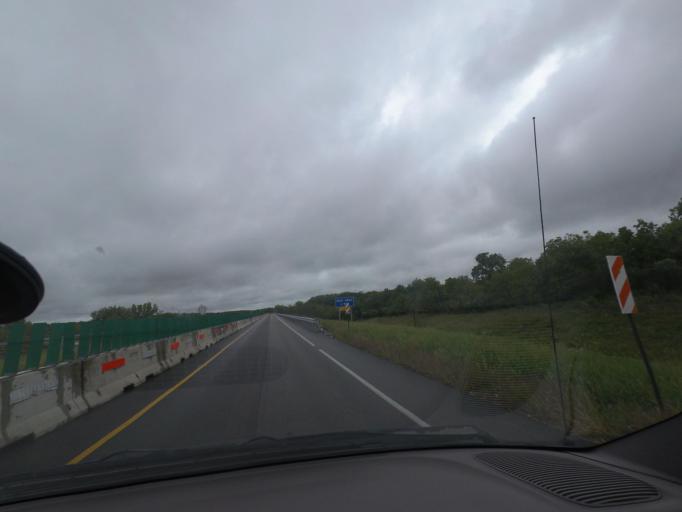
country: US
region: Illinois
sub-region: Piatt County
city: Cerro Gordo
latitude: 39.9777
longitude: -88.7984
